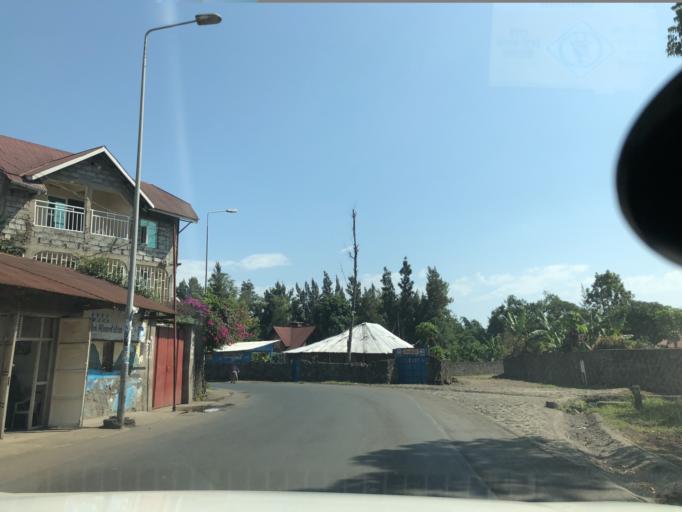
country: CD
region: Nord Kivu
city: Goma
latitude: -1.6617
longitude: 29.1732
